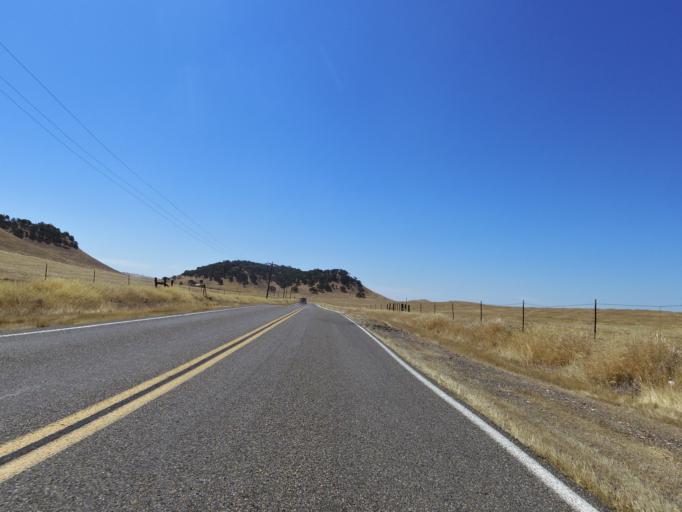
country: US
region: California
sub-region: Merced County
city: Planada
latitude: 37.4929
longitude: -120.3057
